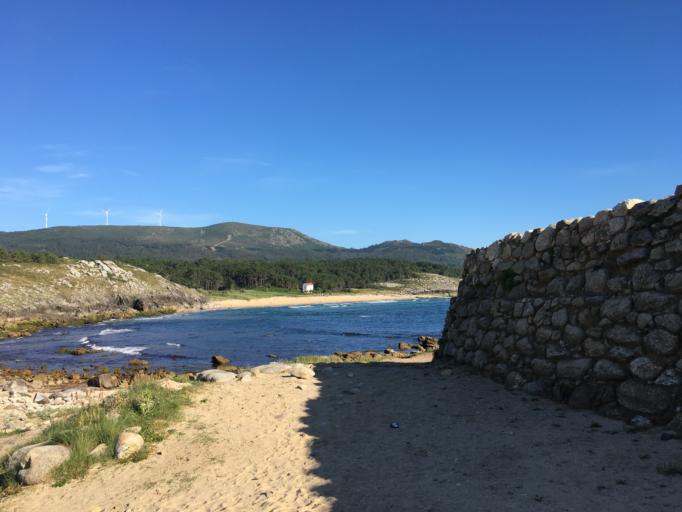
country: ES
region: Galicia
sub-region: Provincia da Coruna
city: Porto do Son
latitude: 42.6946
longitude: -9.0314
